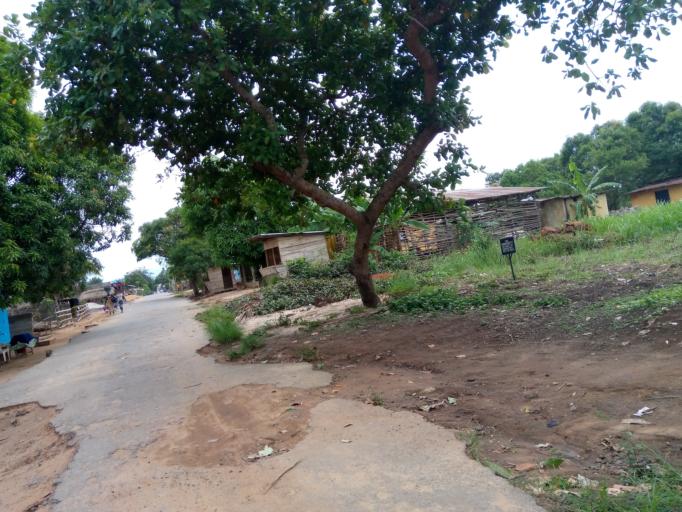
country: SL
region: Western Area
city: Waterloo
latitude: 8.3343
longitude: -13.0194
